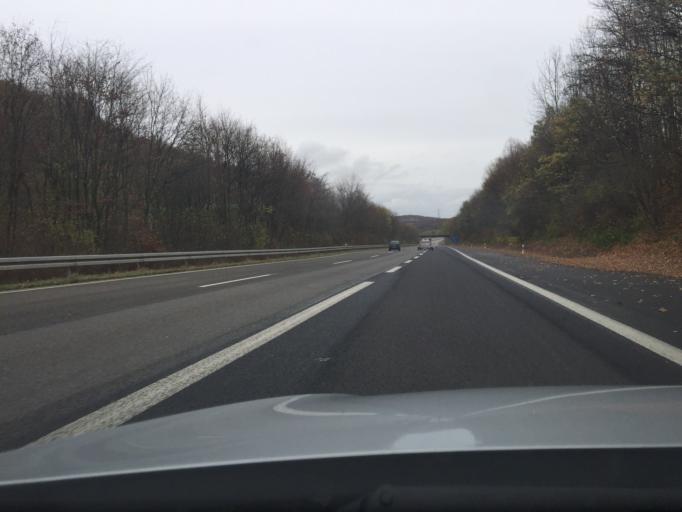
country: DE
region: North Rhine-Westphalia
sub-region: Regierungsbezirk Dusseldorf
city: Velbert
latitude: 51.3557
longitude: 7.0466
